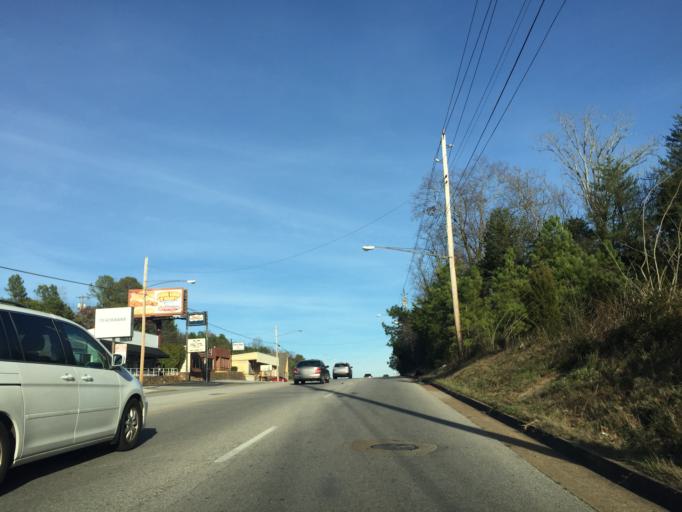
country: US
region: Tennessee
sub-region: Hamilton County
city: Red Bank
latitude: 35.1116
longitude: -85.2689
